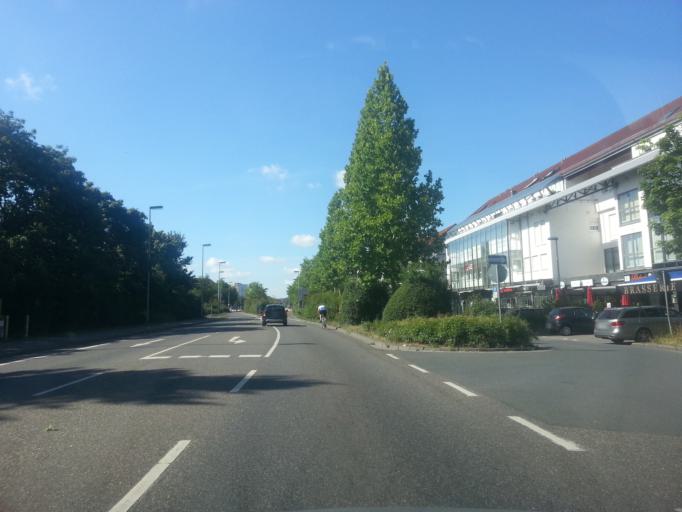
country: DE
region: Hesse
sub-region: Regierungsbezirk Darmstadt
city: Dietzenbach
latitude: 50.0250
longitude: 8.7843
